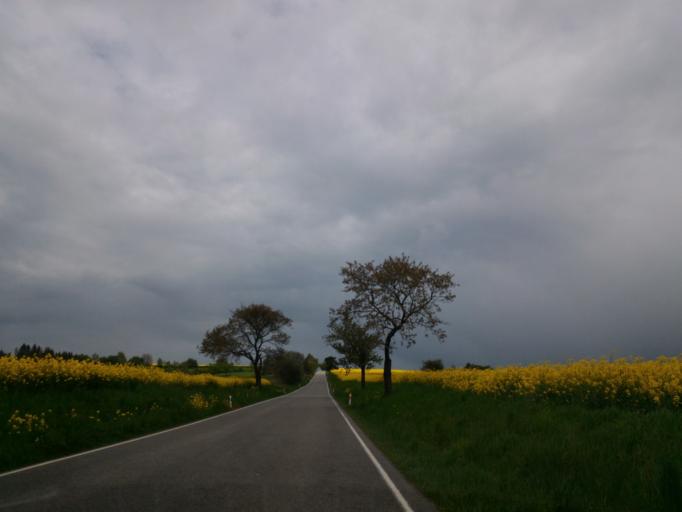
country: CZ
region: Vysocina
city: Ledec nad Sazavou
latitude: 49.7204
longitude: 15.2679
